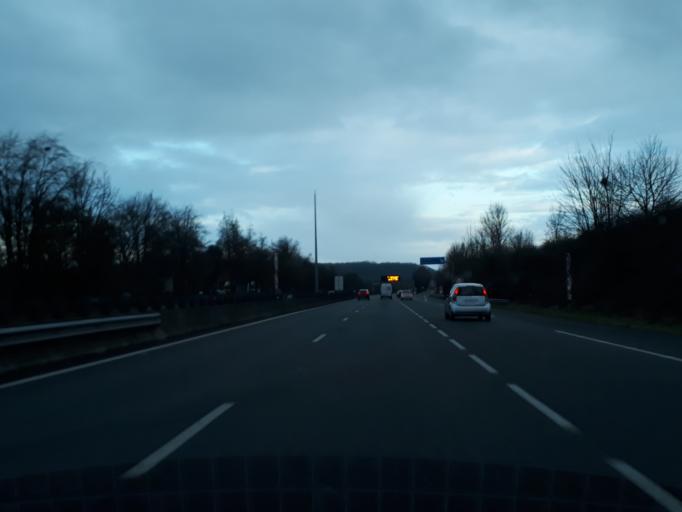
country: FR
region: Picardie
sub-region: Departement de l'Oise
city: Verberie
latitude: 49.2840
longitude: 2.6942
